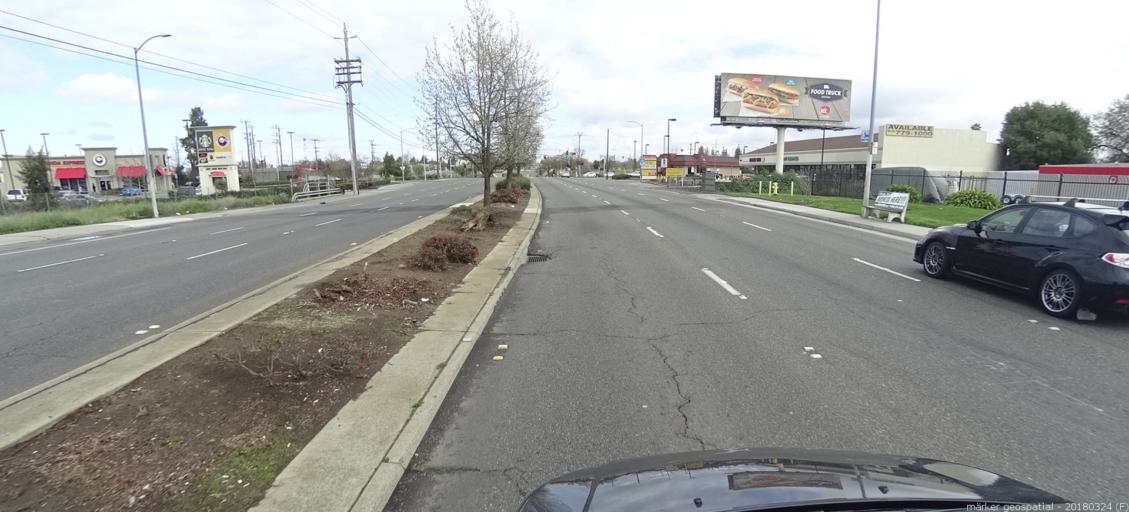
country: US
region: California
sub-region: Sacramento County
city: North Highlands
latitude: 38.6560
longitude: -121.3829
